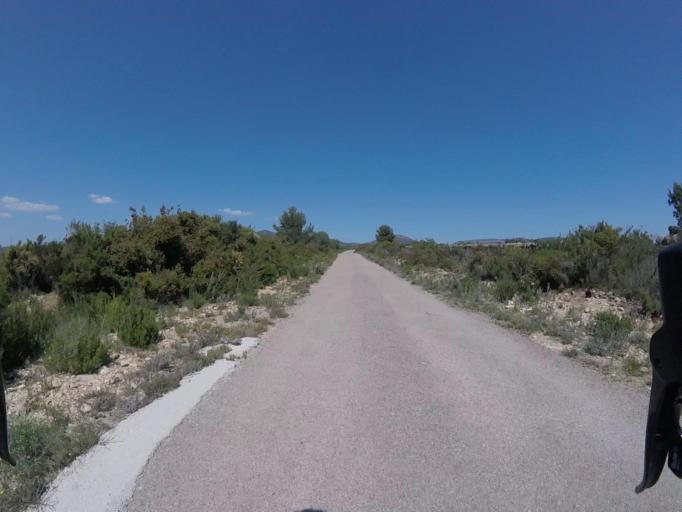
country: ES
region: Valencia
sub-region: Provincia de Castello
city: Sierra-Engarceran
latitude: 40.2275
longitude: -0.0231
